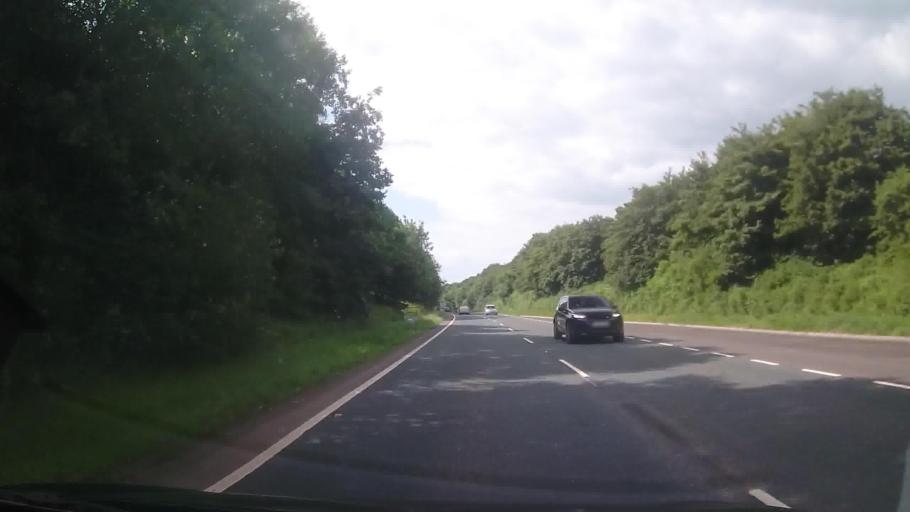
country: GB
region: England
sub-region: Shropshire
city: Ludlow
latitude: 52.3728
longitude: -2.6982
